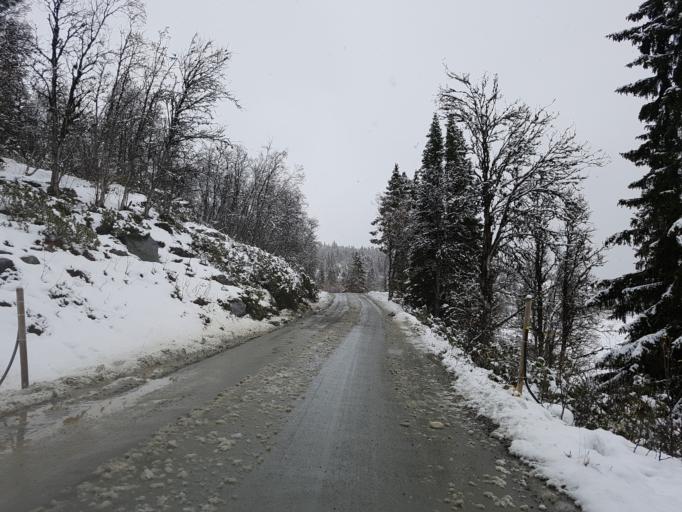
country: NO
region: Oppland
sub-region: Sel
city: Otta
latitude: 61.8021
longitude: 9.7039
